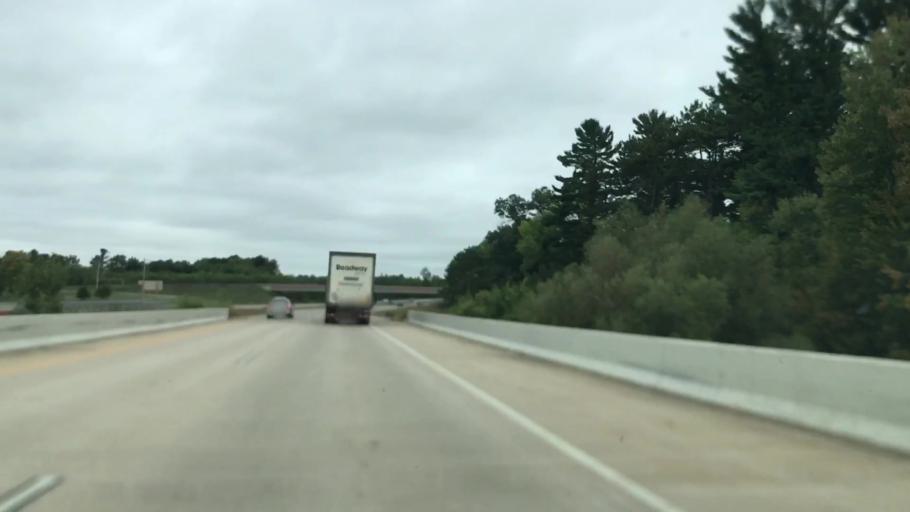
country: US
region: Wisconsin
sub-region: Marinette County
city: Peshtigo
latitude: 45.0396
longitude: -87.7427
